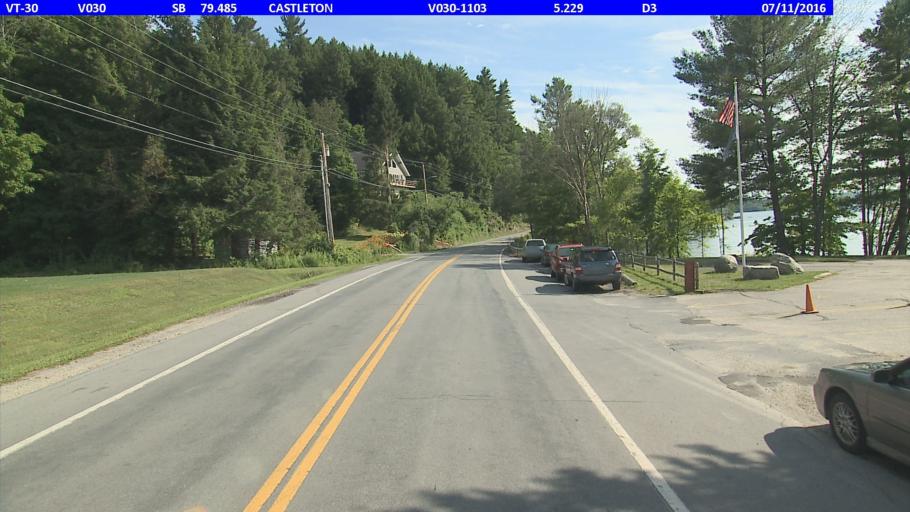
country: US
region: Vermont
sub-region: Rutland County
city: Castleton
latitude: 43.6601
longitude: -73.1902
